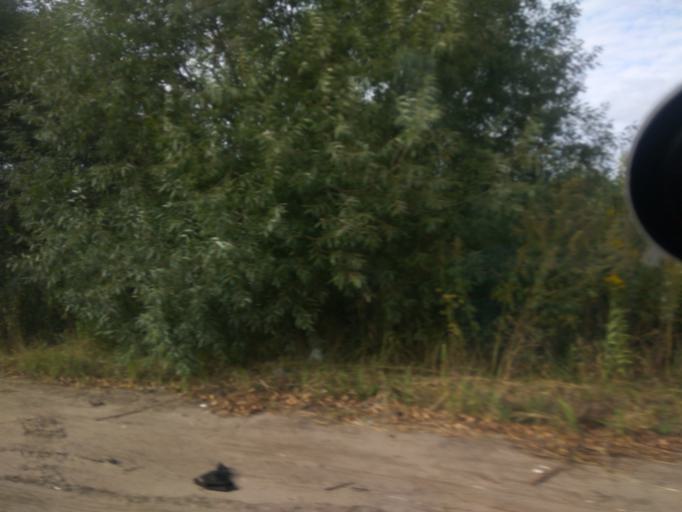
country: RU
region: Moskovskaya
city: Ramenskoye
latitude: 55.5672
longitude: 38.2663
